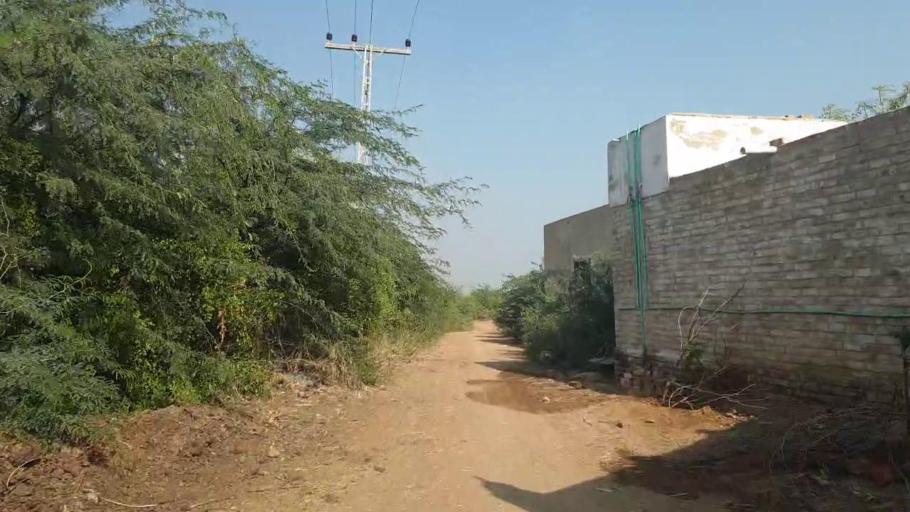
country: PK
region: Sindh
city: Jamshoro
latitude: 25.4508
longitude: 68.2897
